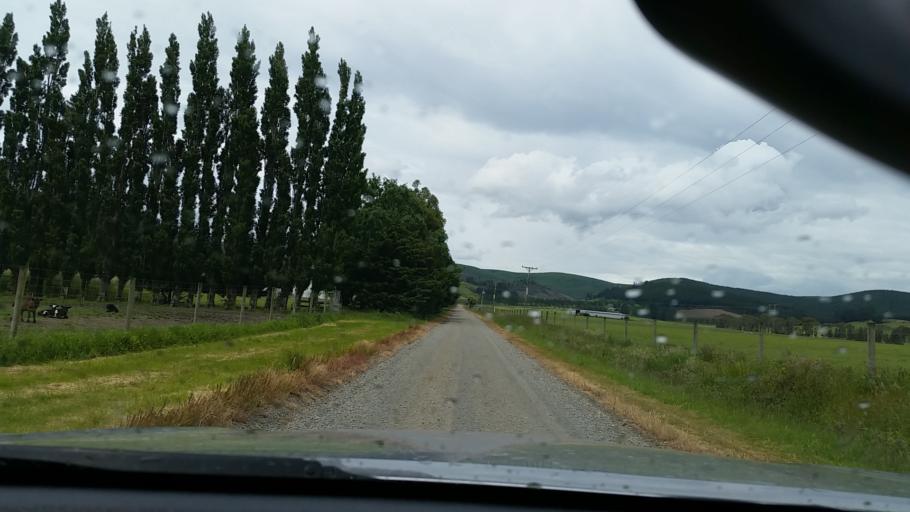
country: NZ
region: Southland
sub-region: Southland District
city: Winton
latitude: -45.9094
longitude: 168.1533
